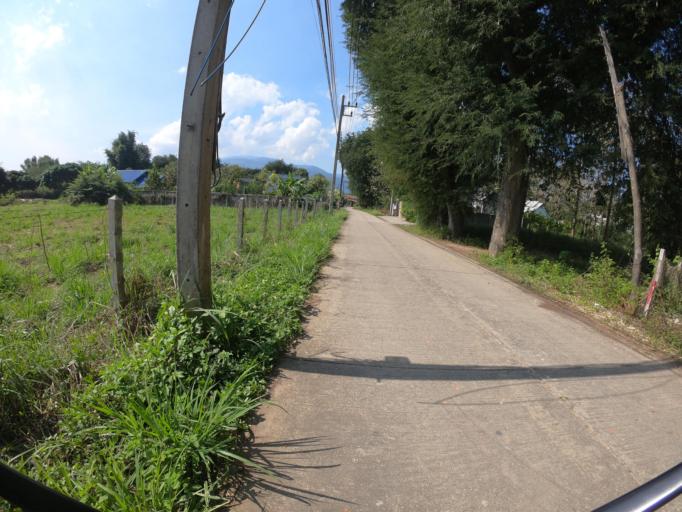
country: TH
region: Chiang Mai
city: San Sai
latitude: 18.8712
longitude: 98.9776
